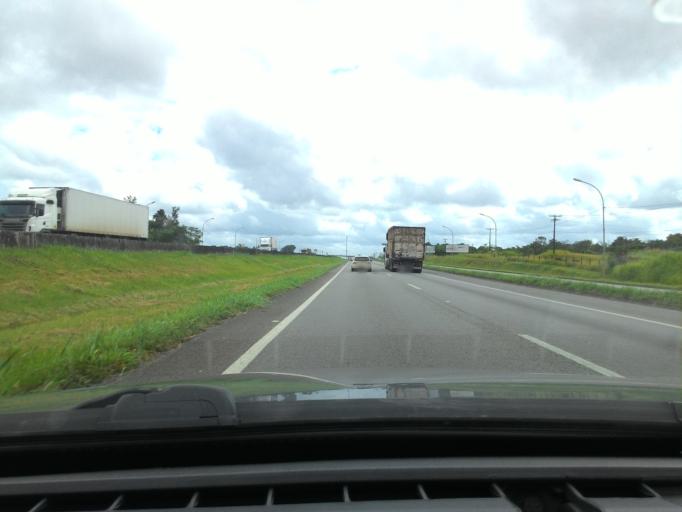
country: BR
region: Sao Paulo
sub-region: Registro
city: Registro
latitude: -24.5372
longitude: -47.8590
